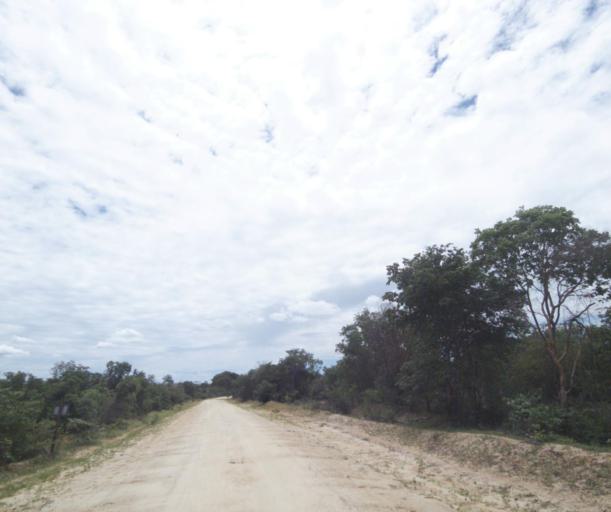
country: BR
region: Bahia
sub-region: Carinhanha
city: Carinhanha
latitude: -14.2100
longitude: -43.9161
